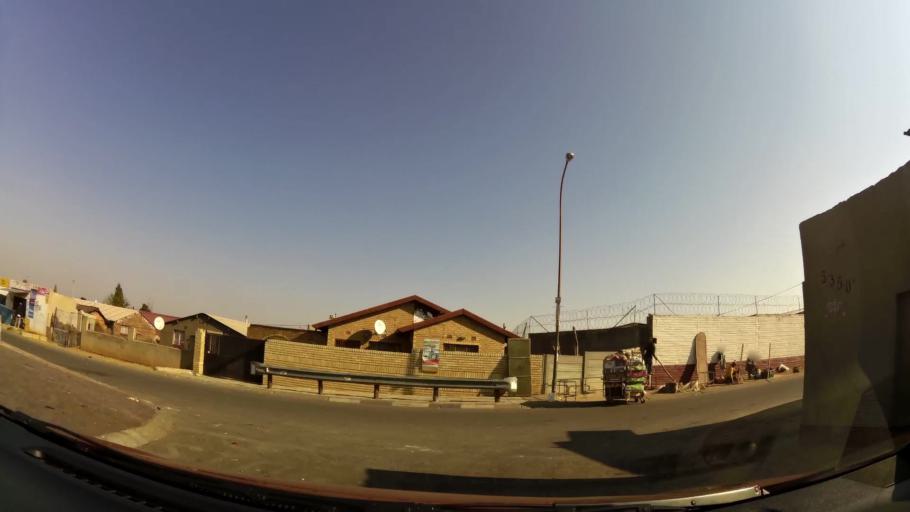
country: ZA
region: Gauteng
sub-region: City of Johannesburg Metropolitan Municipality
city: Soweto
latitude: -26.2499
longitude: 27.9516
